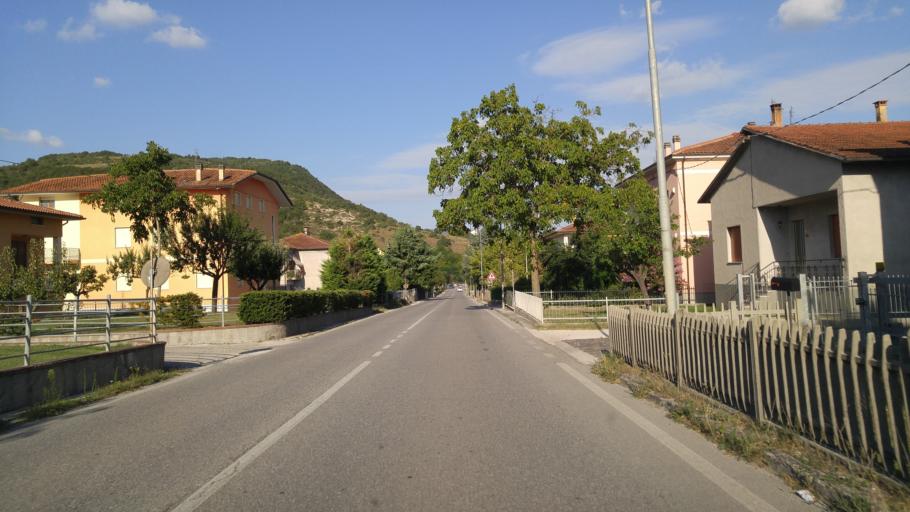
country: IT
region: The Marches
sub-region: Provincia di Pesaro e Urbino
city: Acqualagna
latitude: 43.6135
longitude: 12.6353
